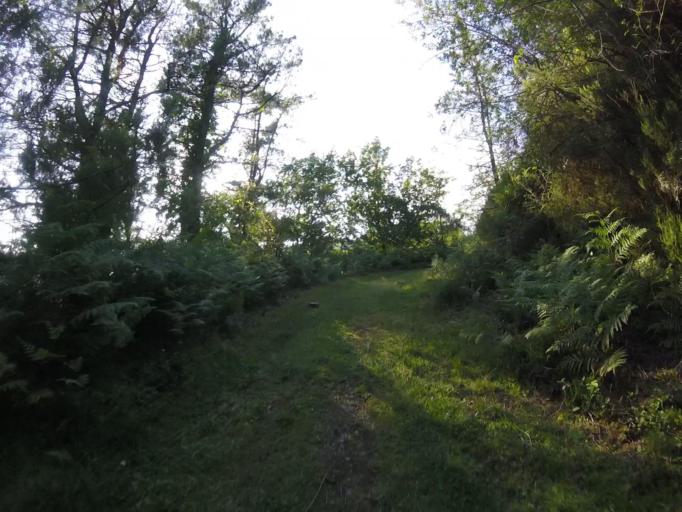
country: ES
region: Navarre
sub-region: Provincia de Navarra
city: Arano
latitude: 43.2273
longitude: -1.9069
